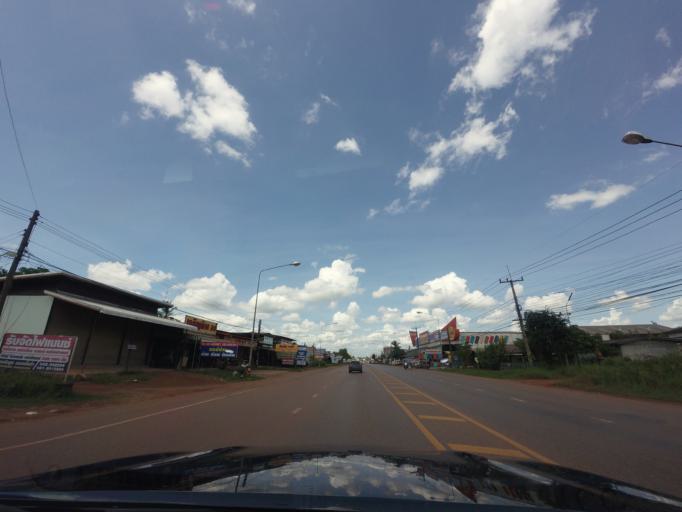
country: TH
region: Changwat Udon Thani
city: Ban Dung
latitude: 17.6822
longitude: 103.2552
